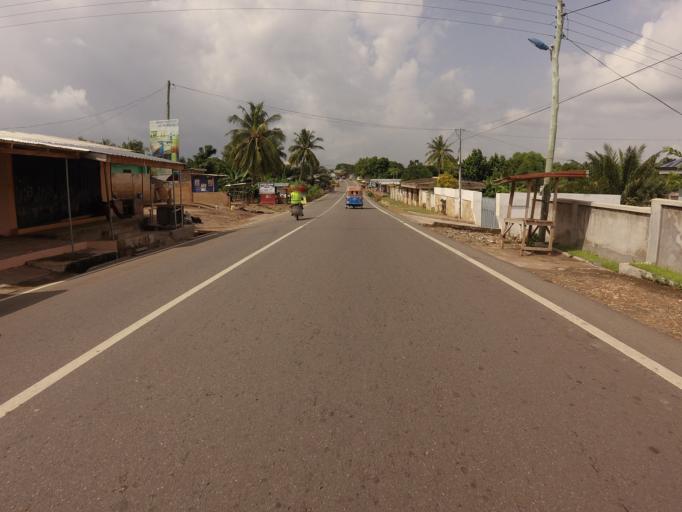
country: GH
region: Volta
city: Ho
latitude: 6.6212
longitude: 0.4788
